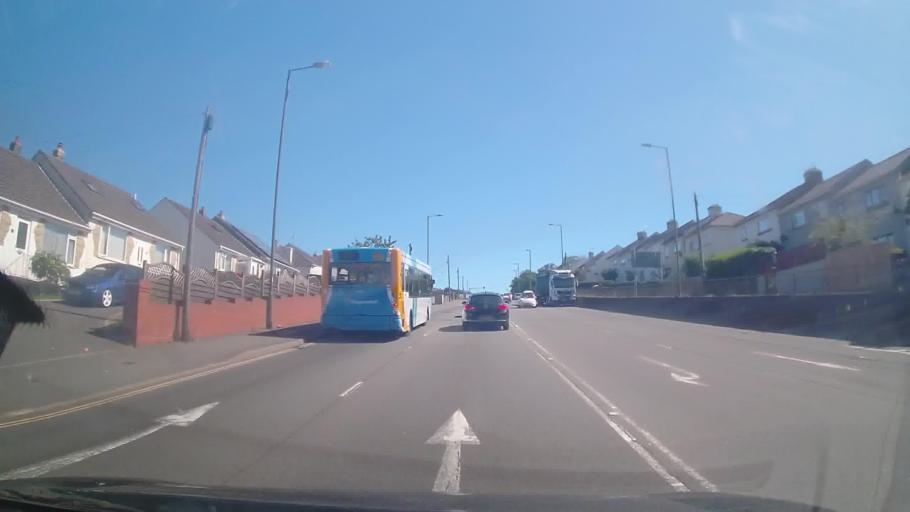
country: GB
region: England
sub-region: Borough of Torbay
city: Paignton
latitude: 50.4279
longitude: -3.5885
